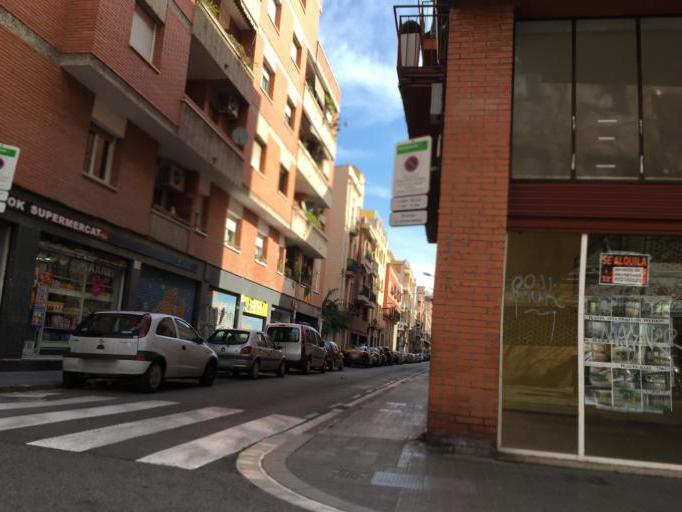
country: ES
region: Catalonia
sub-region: Provincia de Barcelona
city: les Corts
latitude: 41.3812
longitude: 2.1368
